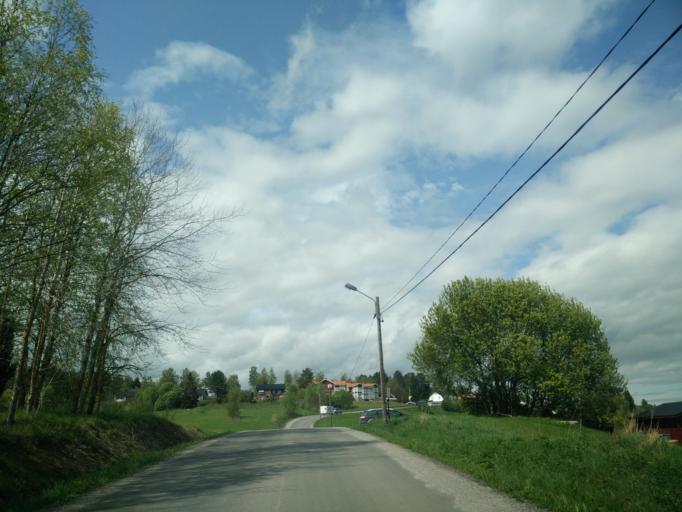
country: SE
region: Vaesternorrland
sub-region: Sundsvalls Kommun
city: Sundsvall
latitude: 62.3677
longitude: 17.2690
